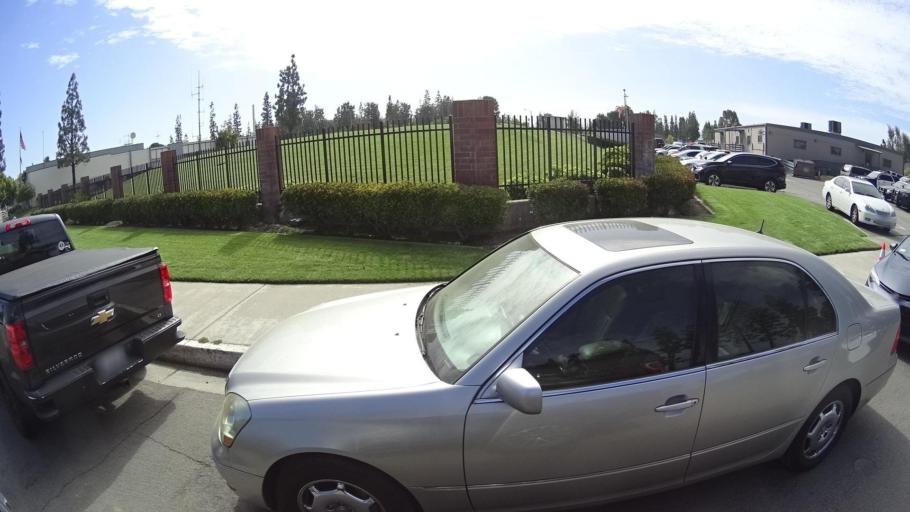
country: US
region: California
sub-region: Los Angeles County
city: La Puente
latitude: 34.0246
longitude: -117.9598
